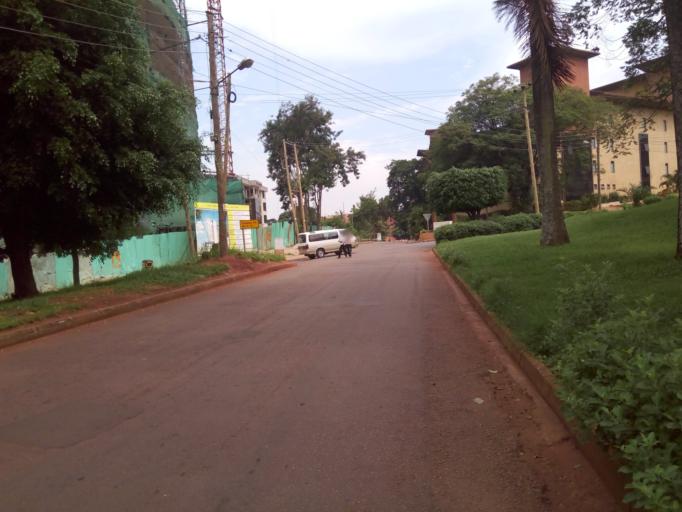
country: UG
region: Central Region
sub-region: Kampala District
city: Kampala
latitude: 0.3222
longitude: 32.5844
